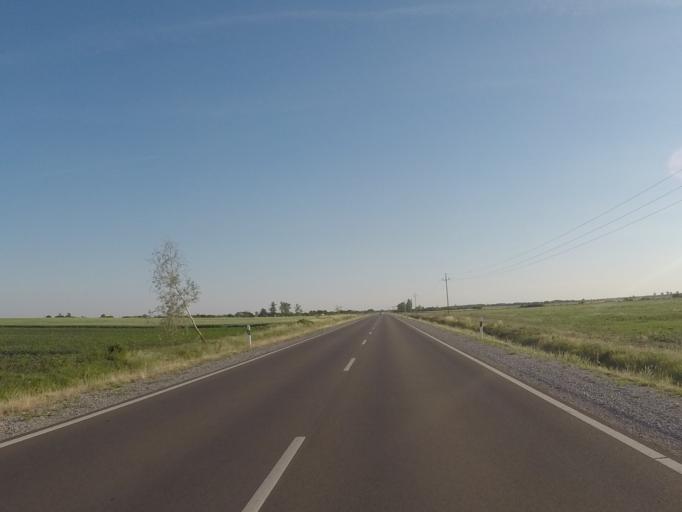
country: HU
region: Heves
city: Besenyotelek
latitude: 47.6932
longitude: 20.3950
